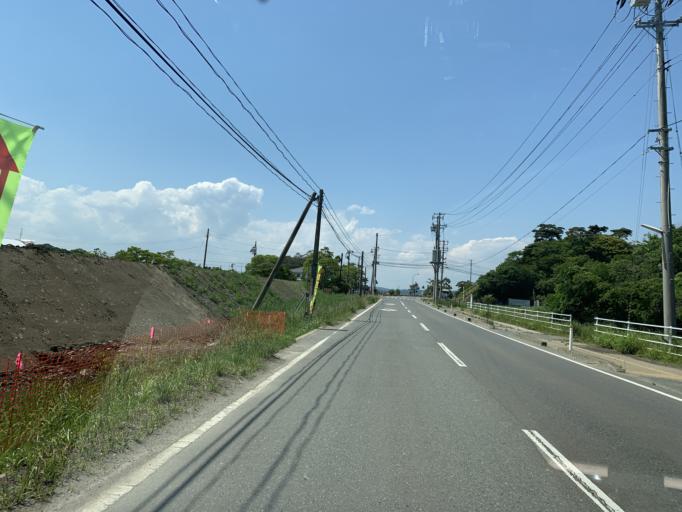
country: JP
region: Miyagi
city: Matsushima
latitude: 38.3372
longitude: 141.1495
